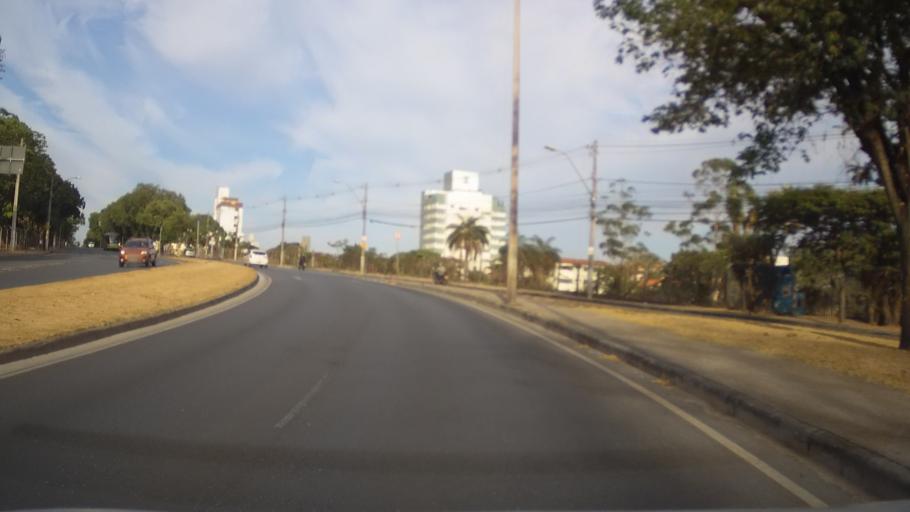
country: BR
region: Minas Gerais
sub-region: Belo Horizonte
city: Belo Horizonte
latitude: -19.8599
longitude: -43.9608
